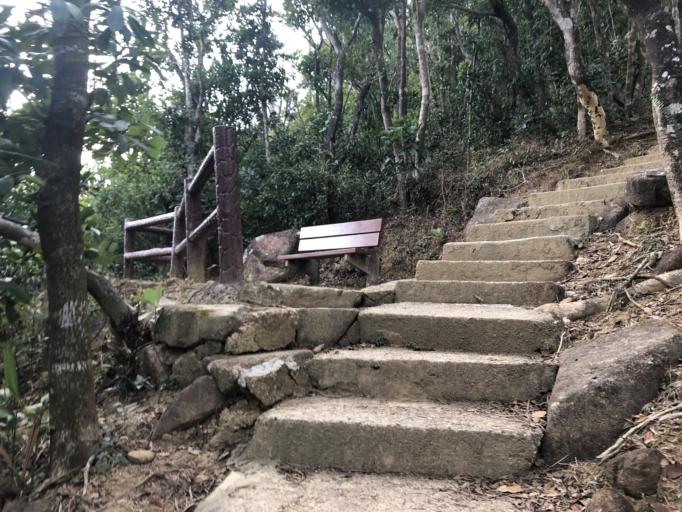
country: HK
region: Wanchai
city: Wan Chai
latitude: 22.2672
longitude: 114.2125
